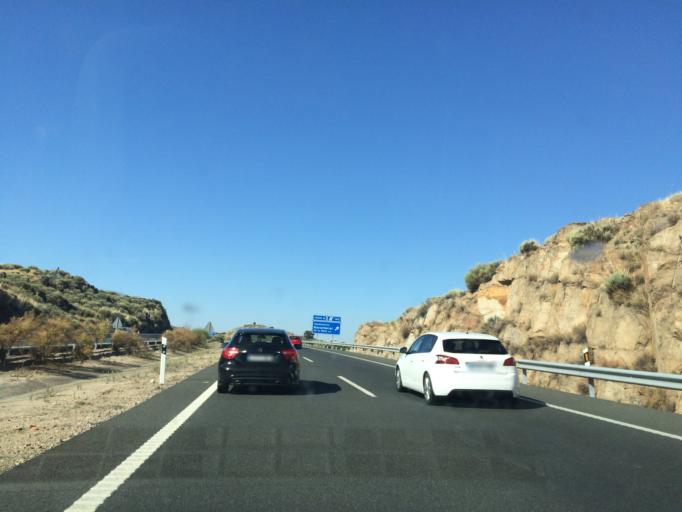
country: ES
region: Extremadura
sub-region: Provincia de Caceres
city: Navalmoral de la Mata
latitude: 39.8834
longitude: -5.5351
